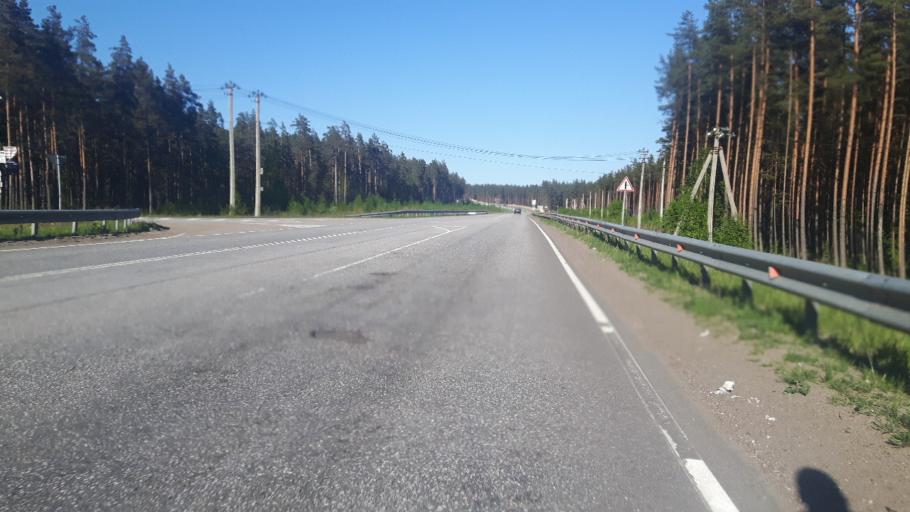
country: RU
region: Leningrad
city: Molodezhnoye
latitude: 60.1693
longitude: 29.2711
